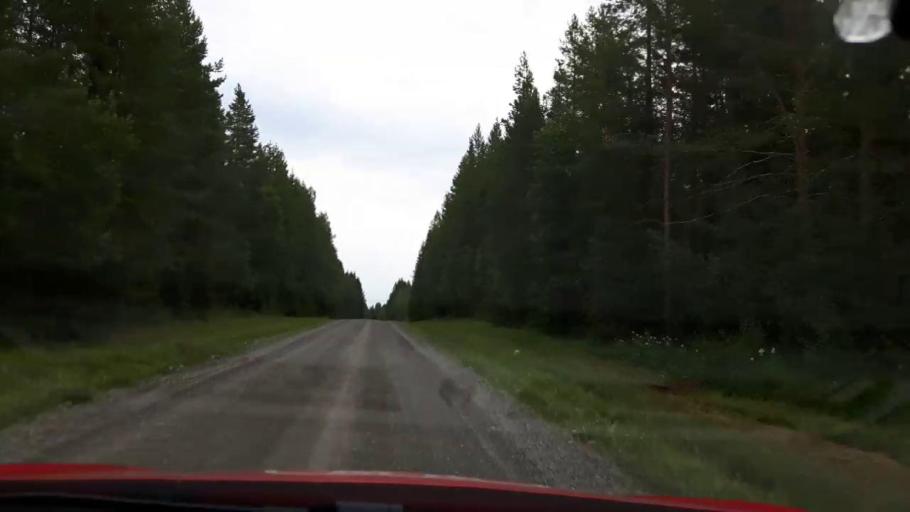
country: SE
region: Jaemtland
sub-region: Stroemsunds Kommun
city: Stroemsund
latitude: 63.7174
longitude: 15.5178
